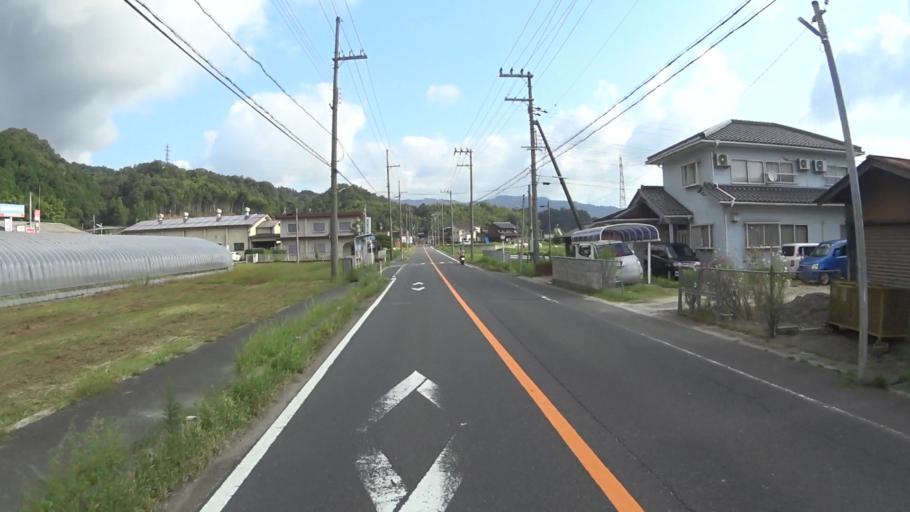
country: JP
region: Kyoto
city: Miyazu
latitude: 35.5577
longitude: 135.1398
